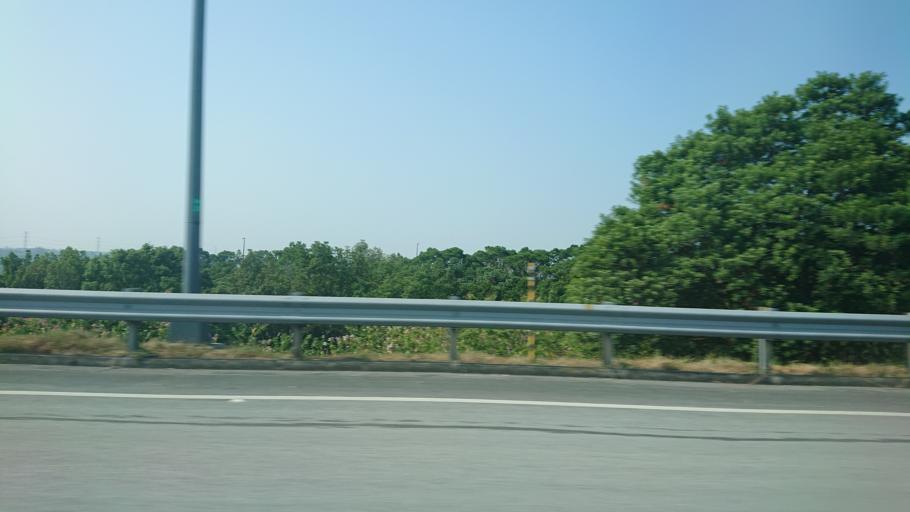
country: TW
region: Taiwan
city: Lugu
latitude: 23.7968
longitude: 120.7014
